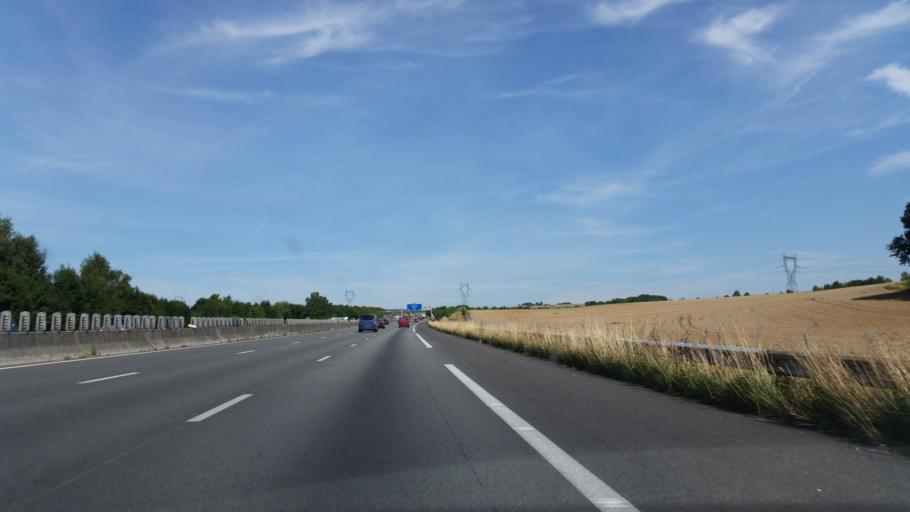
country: FR
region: Picardie
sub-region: Departement de la Somme
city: Peronne
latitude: 49.9630
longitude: 2.8572
